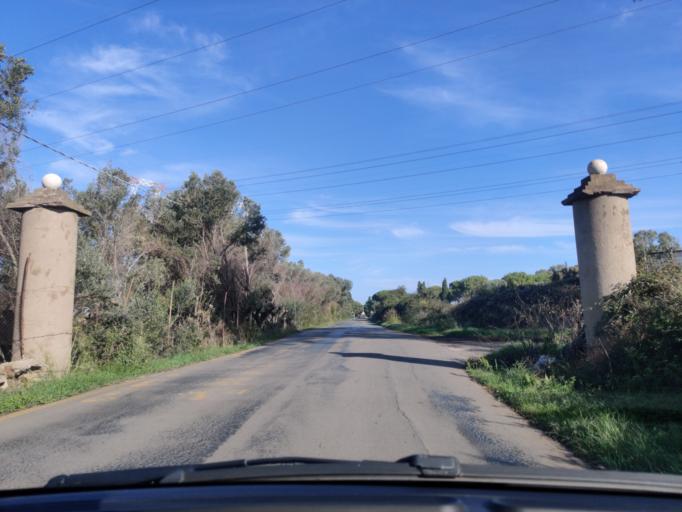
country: IT
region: Latium
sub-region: Citta metropolitana di Roma Capitale
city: Aurelia
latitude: 42.1314
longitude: 11.7878
